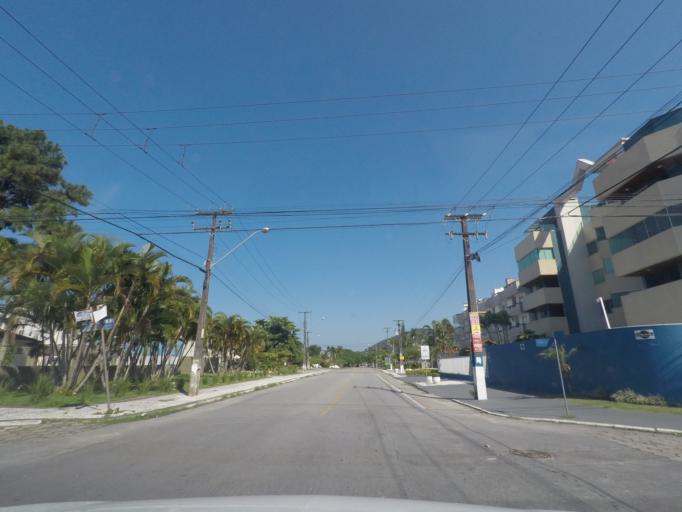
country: BR
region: Parana
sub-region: Guaratuba
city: Guaratuba
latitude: -25.8317
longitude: -48.5396
